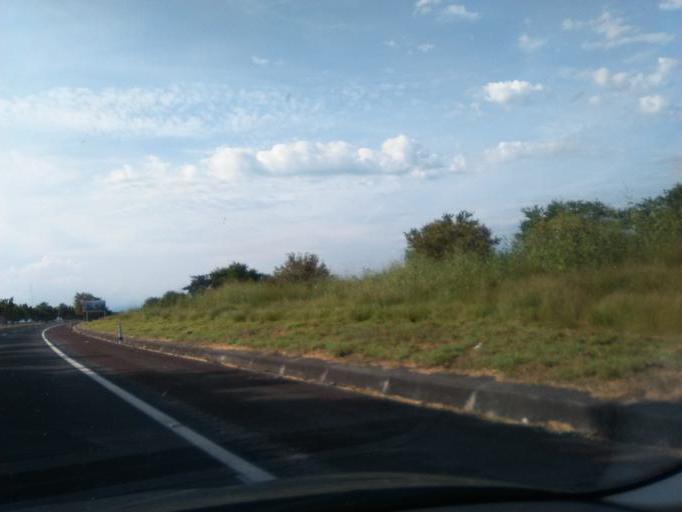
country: MX
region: Morelos
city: Puente de Ixtla
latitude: 18.6018
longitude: -99.2828
